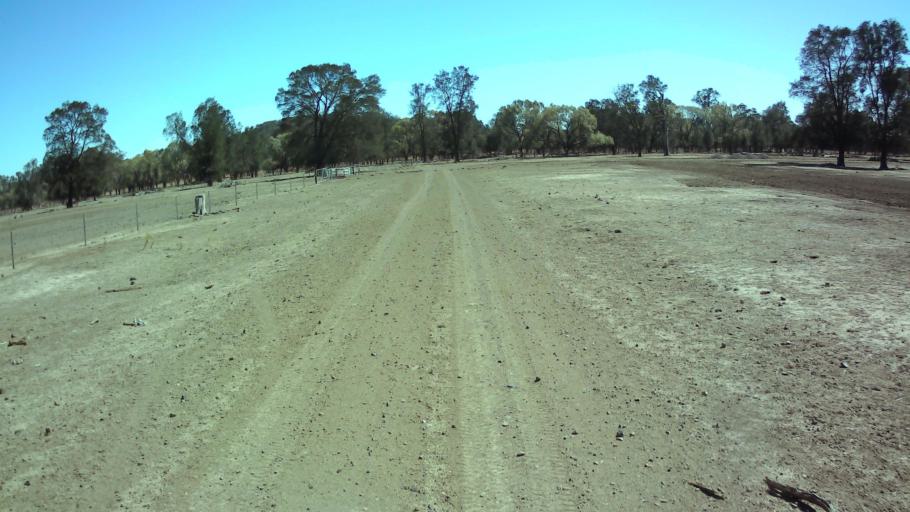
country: AU
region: New South Wales
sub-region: Bland
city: West Wyalong
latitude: -33.7408
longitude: 147.6619
